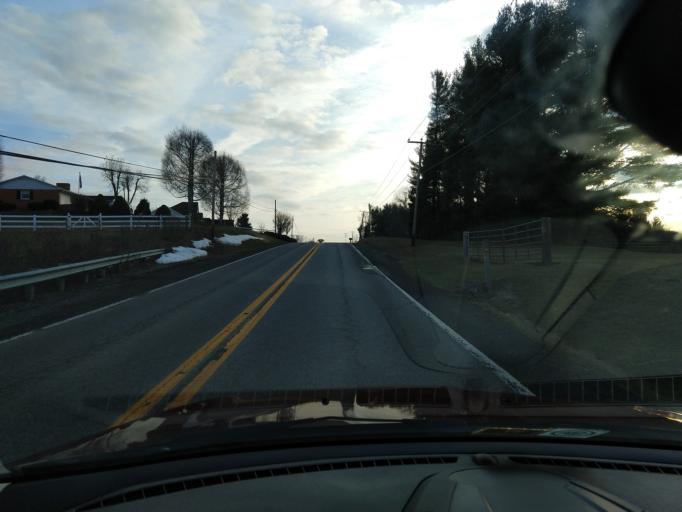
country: US
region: West Virginia
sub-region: Greenbrier County
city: Lewisburg
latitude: 37.9042
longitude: -80.3930
